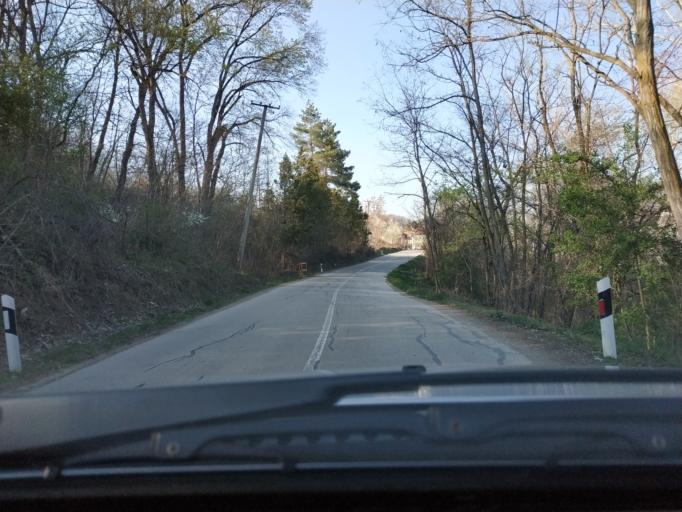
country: RS
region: Central Serbia
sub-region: Nisavski Okrug
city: Aleksinac
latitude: 43.5180
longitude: 21.7995
